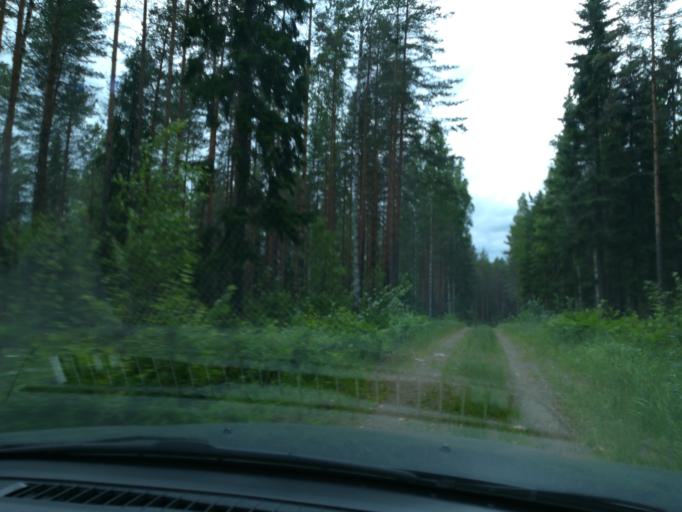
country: FI
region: South Karelia
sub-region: Lappeenranta
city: Savitaipale
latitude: 61.3074
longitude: 27.6178
